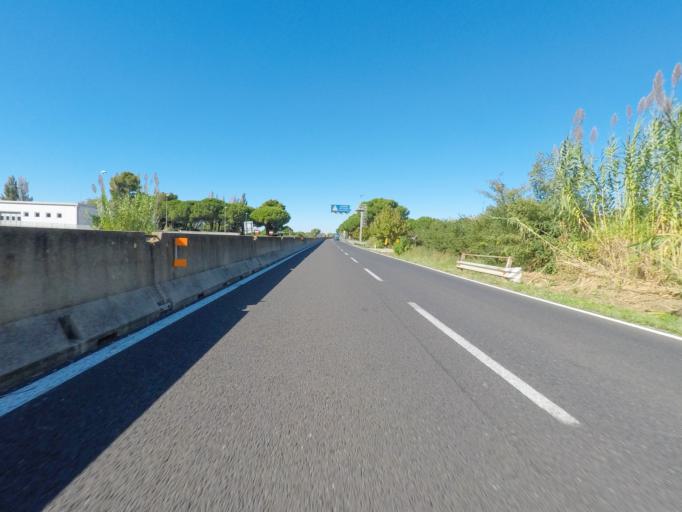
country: IT
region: Tuscany
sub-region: Provincia di Grosseto
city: Orbetello Scalo
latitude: 42.4675
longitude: 11.2394
